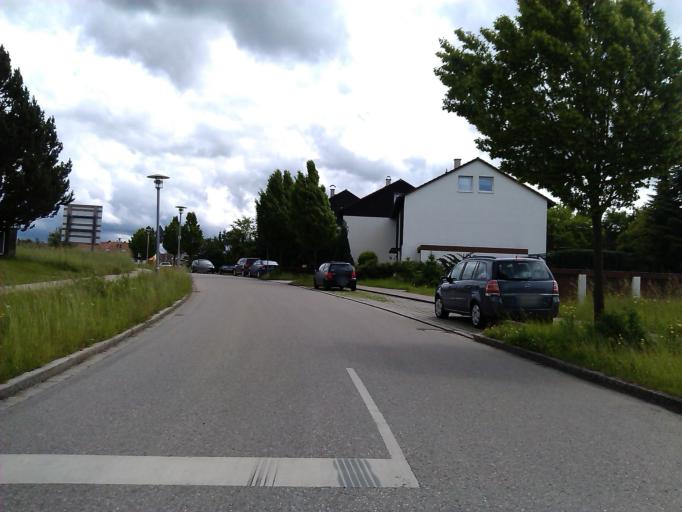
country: DE
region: Bavaria
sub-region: Swabia
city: Marktoberdorf
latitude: 47.7918
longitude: 10.6160
